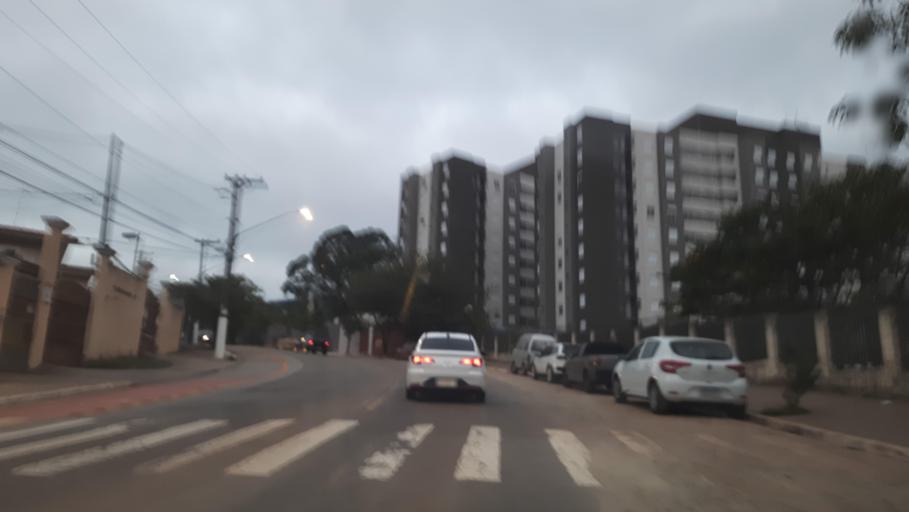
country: BR
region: Sao Paulo
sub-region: Caieiras
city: Caieiras
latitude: -23.4450
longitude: -46.7267
